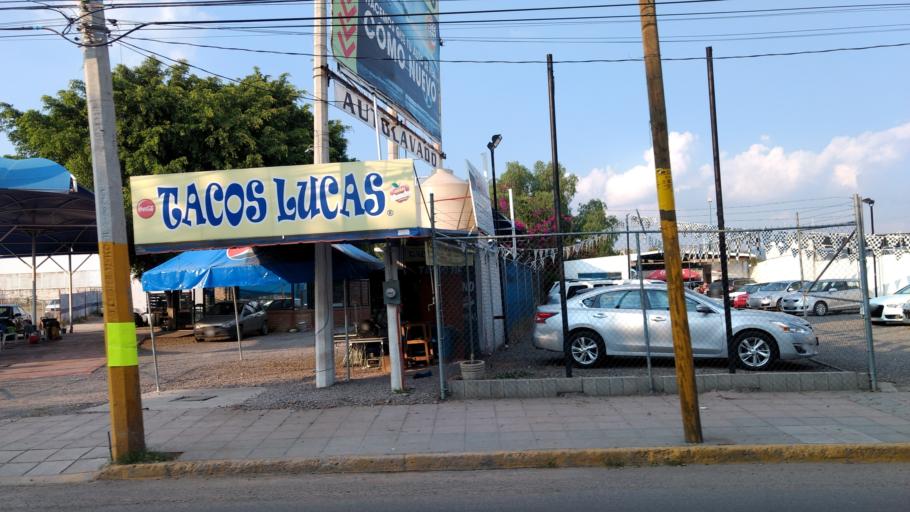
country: MX
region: Guanajuato
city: Leon
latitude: 21.1479
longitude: -101.6754
